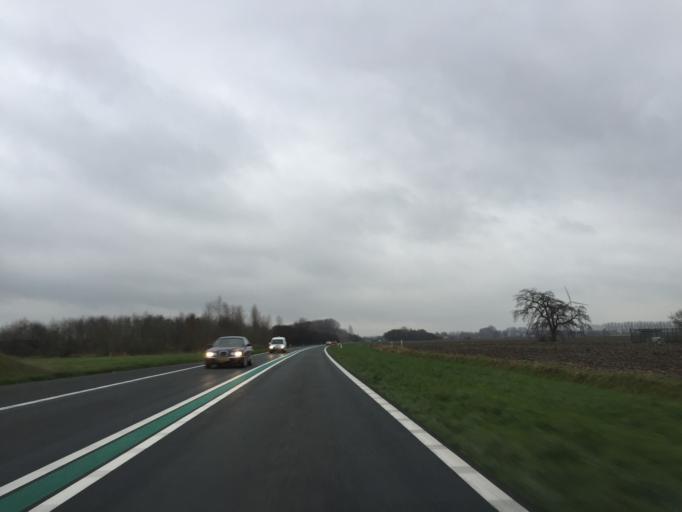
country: NL
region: Zeeland
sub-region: Gemeente Terneuzen
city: Axel
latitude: 51.2827
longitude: 3.8739
